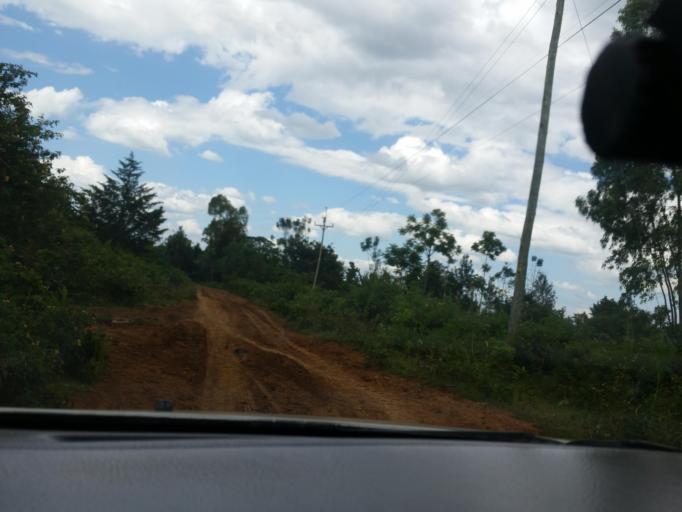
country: KE
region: Siaya
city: Yala
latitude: 0.1000
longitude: 34.4127
